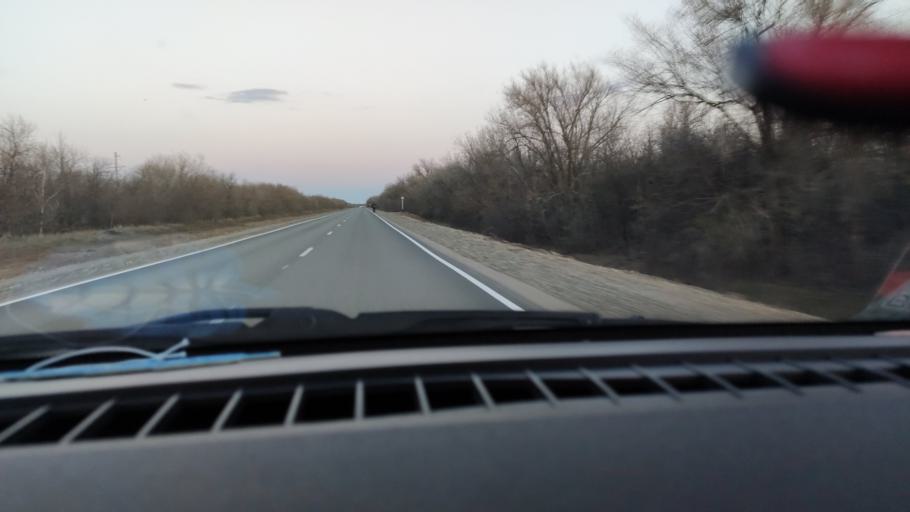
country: RU
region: Saratov
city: Privolzhskiy
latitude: 51.1675
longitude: 45.9439
